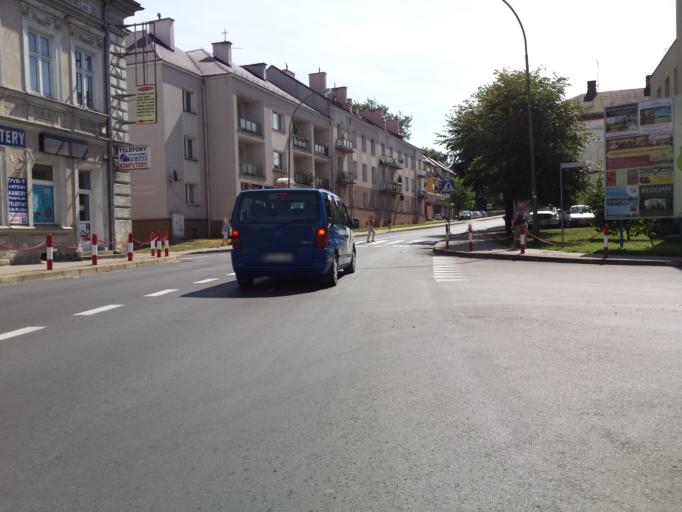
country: PL
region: Subcarpathian Voivodeship
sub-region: Powiat leski
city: Lesko
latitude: 49.4688
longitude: 22.3308
